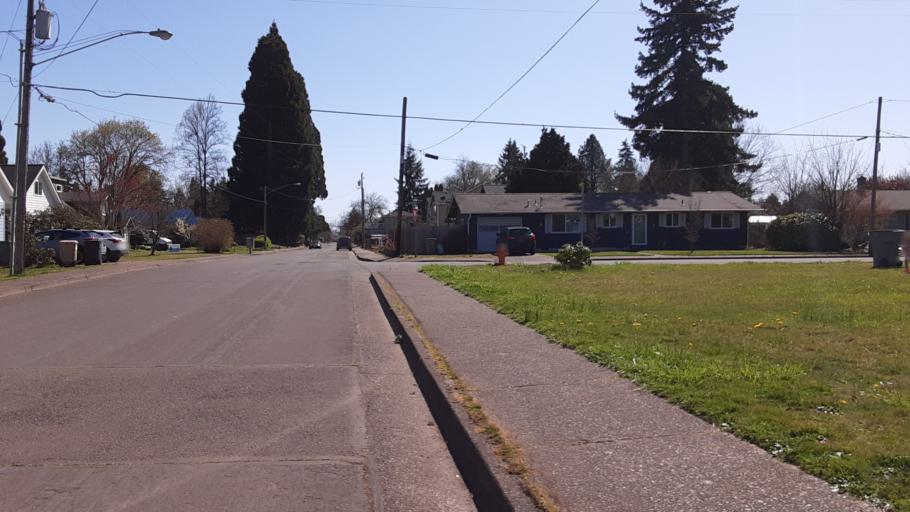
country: US
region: Oregon
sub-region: Benton County
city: Corvallis
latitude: 44.5440
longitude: -123.2605
